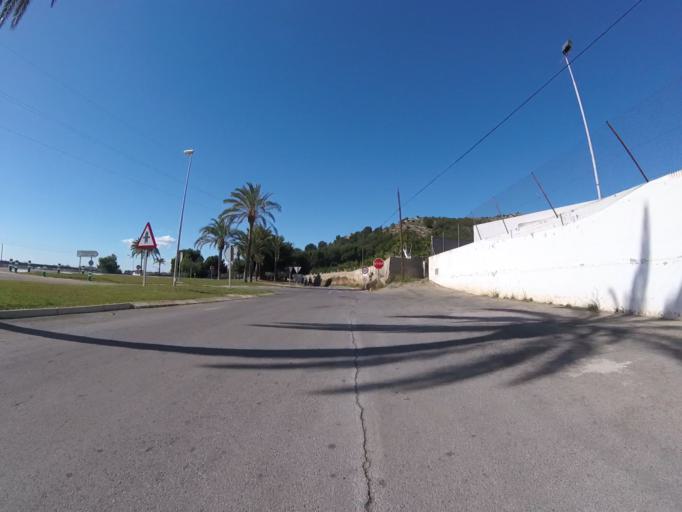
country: ES
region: Valencia
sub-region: Provincia de Castello
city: Benicassim
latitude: 40.0606
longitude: 0.0693
